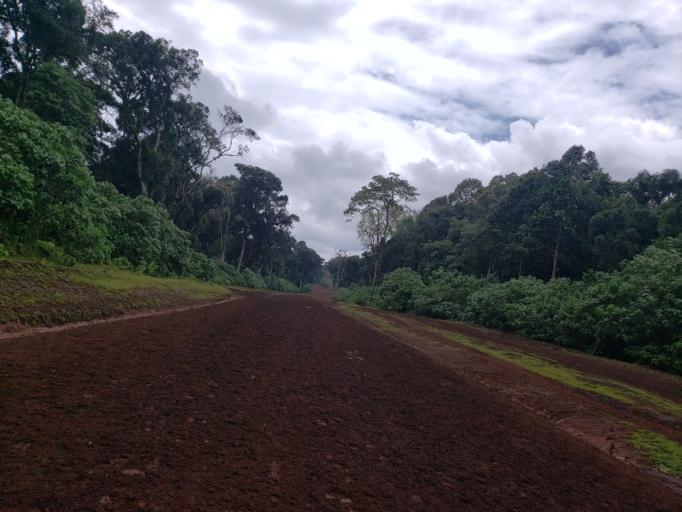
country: ET
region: Oromiya
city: Dodola
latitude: 6.6072
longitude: 39.4170
